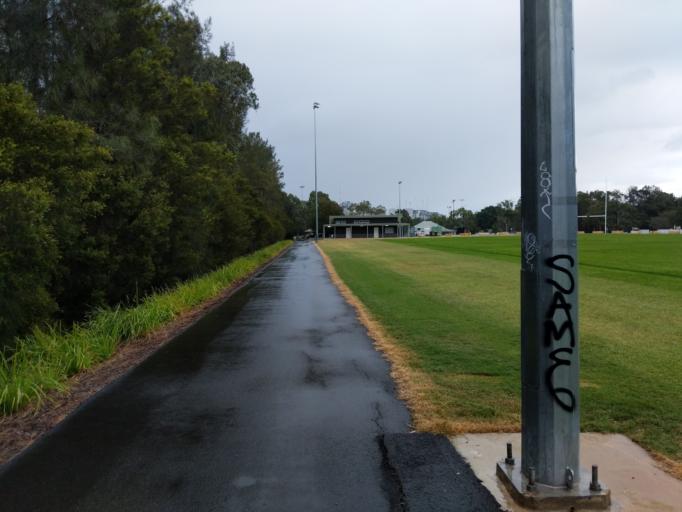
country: AU
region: New South Wales
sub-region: Canada Bay
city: Concord
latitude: -33.8622
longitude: 151.1129
